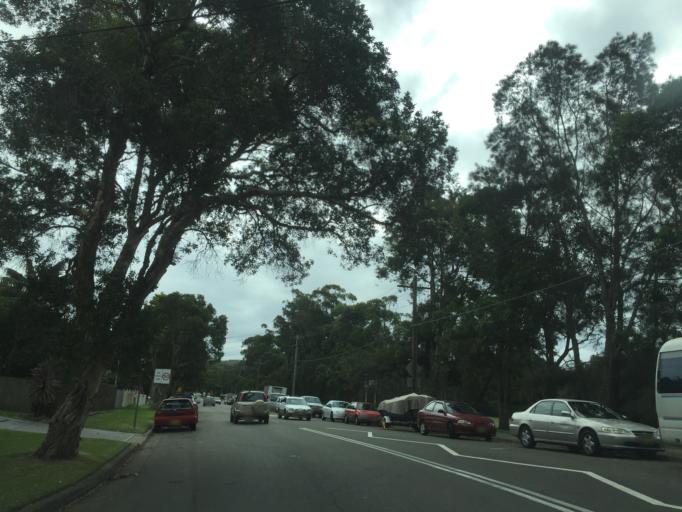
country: AU
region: New South Wales
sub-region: Pittwater
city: North Narrabeen
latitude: -33.6995
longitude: 151.2945
